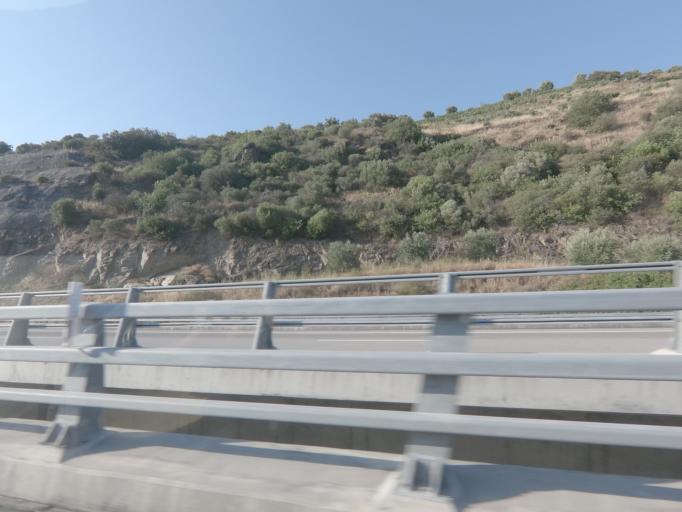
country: PT
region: Vila Real
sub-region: Peso da Regua
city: Peso da Regua
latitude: 41.1732
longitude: -7.7586
